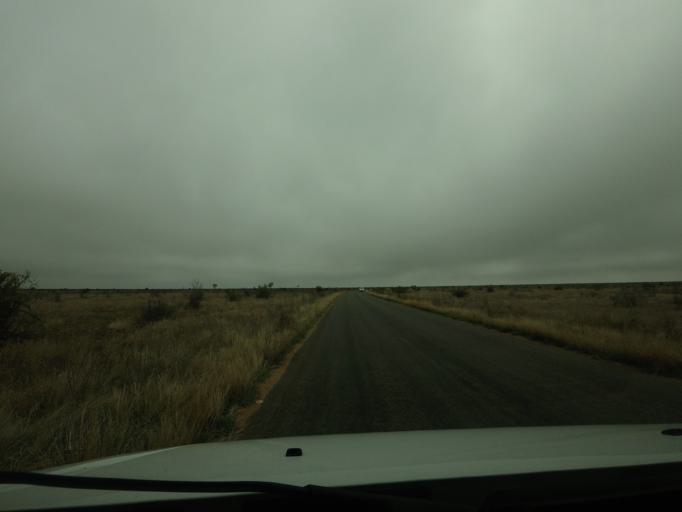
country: ZA
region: Limpopo
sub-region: Mopani District Municipality
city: Phalaborwa
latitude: -24.2375
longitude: 31.7198
